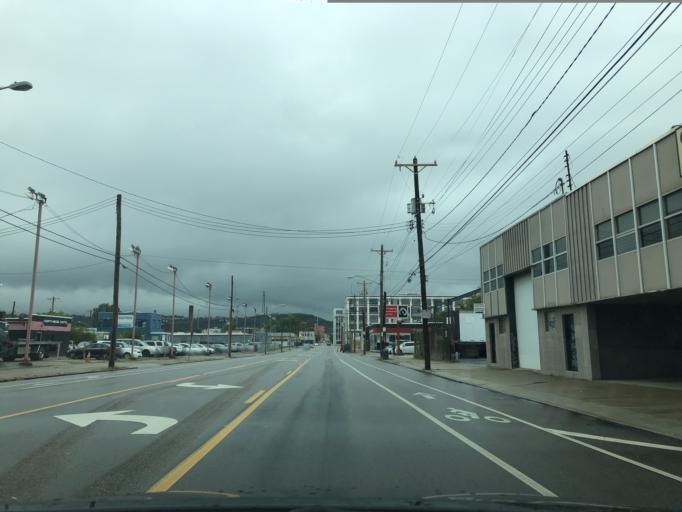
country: US
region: Ohio
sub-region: Hamilton County
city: Saint Bernard
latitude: 39.1597
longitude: -84.5329
